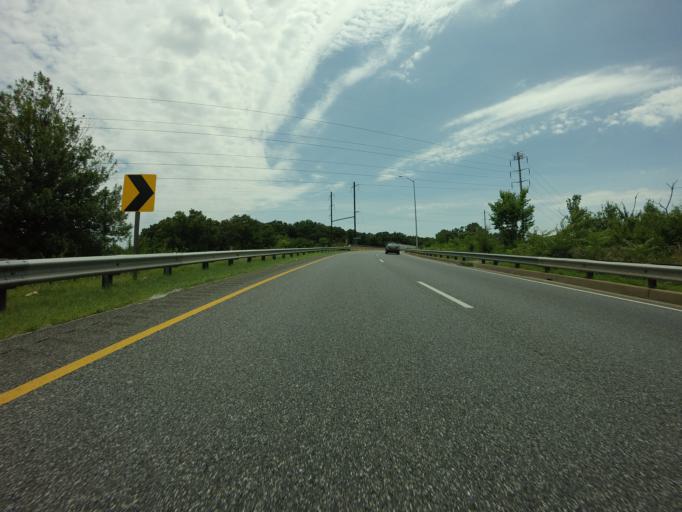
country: US
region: Maryland
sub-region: Baltimore County
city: Rossville
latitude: 39.3264
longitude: -76.4829
